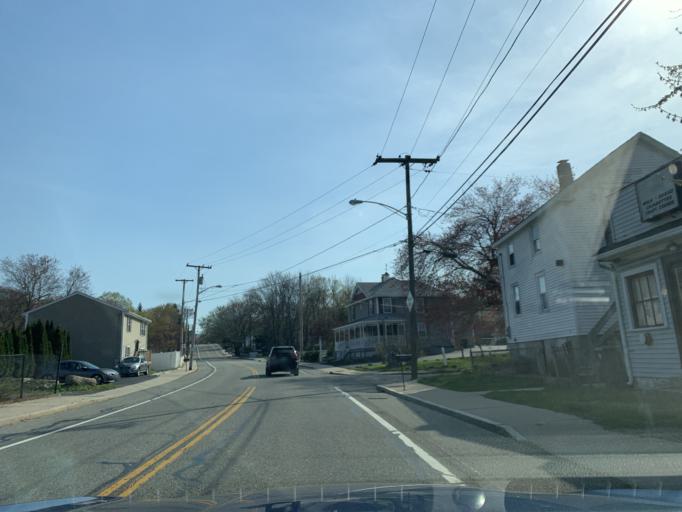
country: US
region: Rhode Island
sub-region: Providence County
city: Johnston
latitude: 41.7988
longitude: -71.5045
